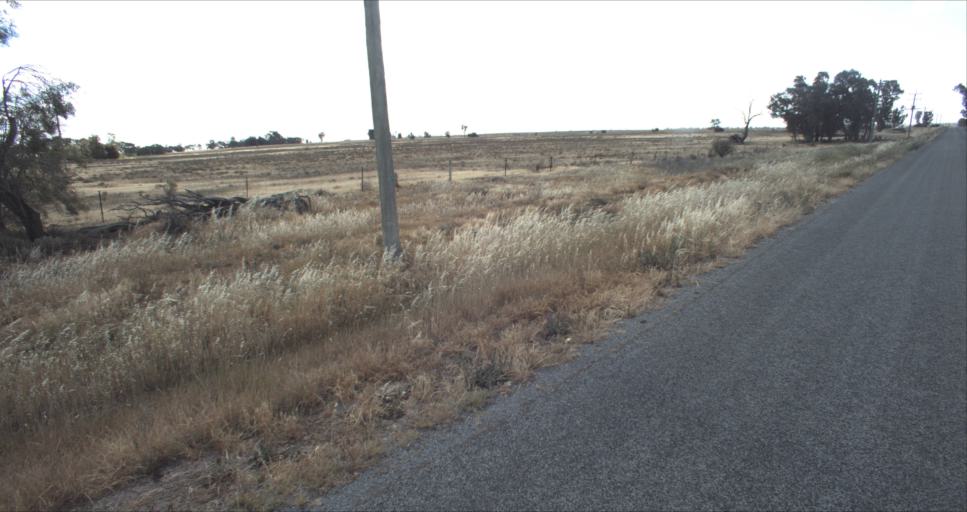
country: AU
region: New South Wales
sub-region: Leeton
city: Leeton
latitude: -34.4873
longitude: 146.2479
